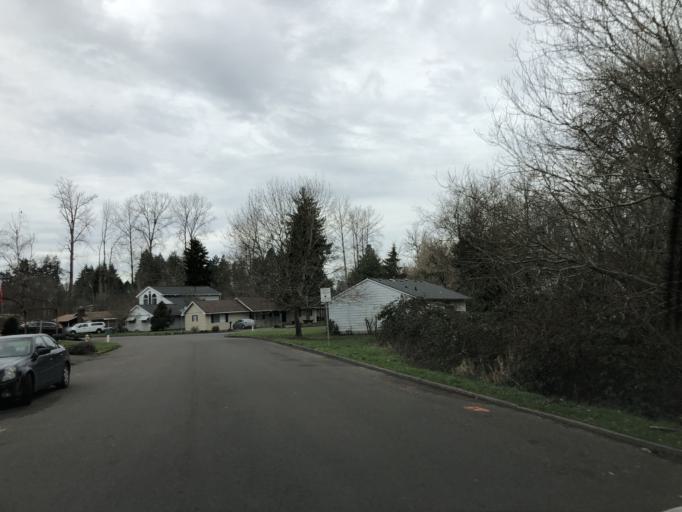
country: US
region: Oregon
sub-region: Washington County
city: Tigard
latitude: 45.4311
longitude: -122.7812
